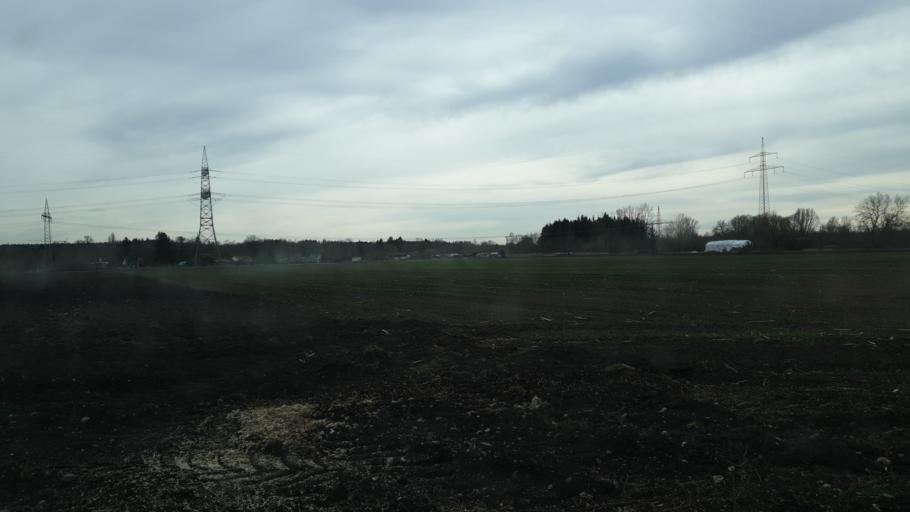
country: DE
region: Bavaria
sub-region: Upper Bavaria
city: Grobenzell
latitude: 48.1791
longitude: 11.3791
